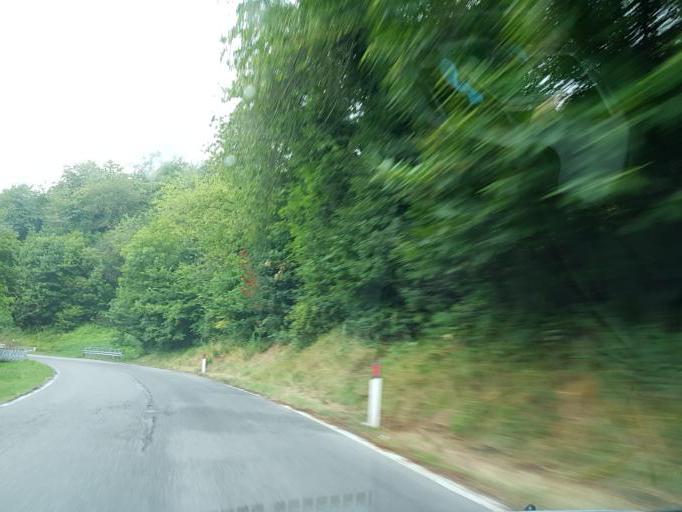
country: IT
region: Piedmont
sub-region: Provincia di Cuneo
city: Tettorosso
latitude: 44.4698
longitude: 7.3180
